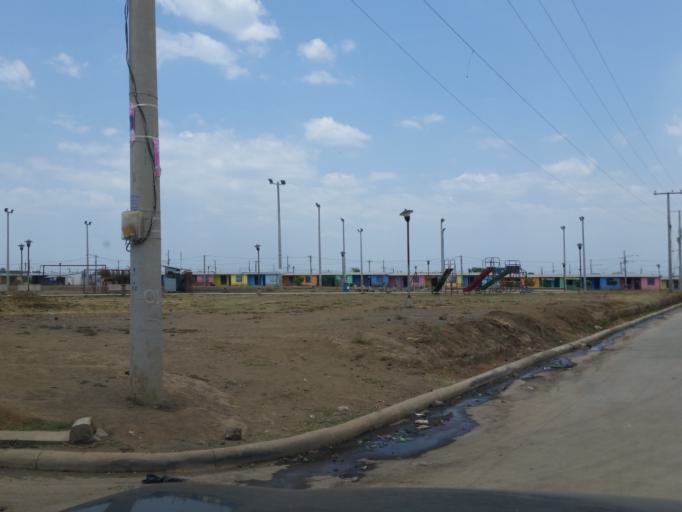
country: NI
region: Managua
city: Tipitapa
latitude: 12.1305
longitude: -86.1572
